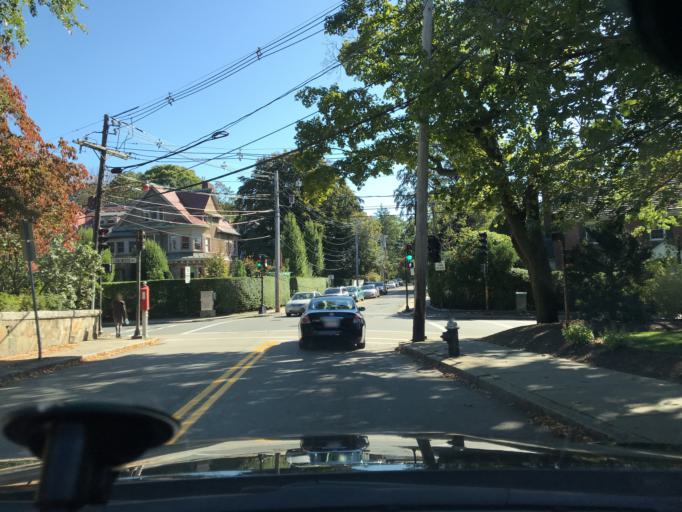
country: US
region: Massachusetts
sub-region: Norfolk County
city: Brookline
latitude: 42.3408
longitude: -71.1127
